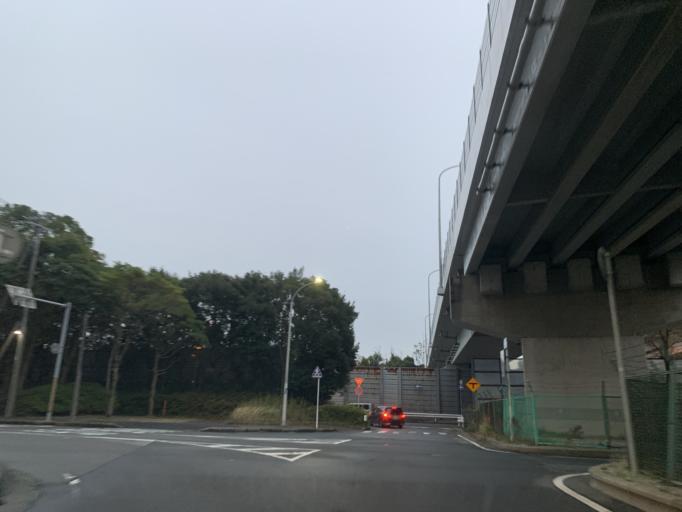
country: JP
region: Chiba
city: Funabashi
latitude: 35.6599
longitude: 140.0335
